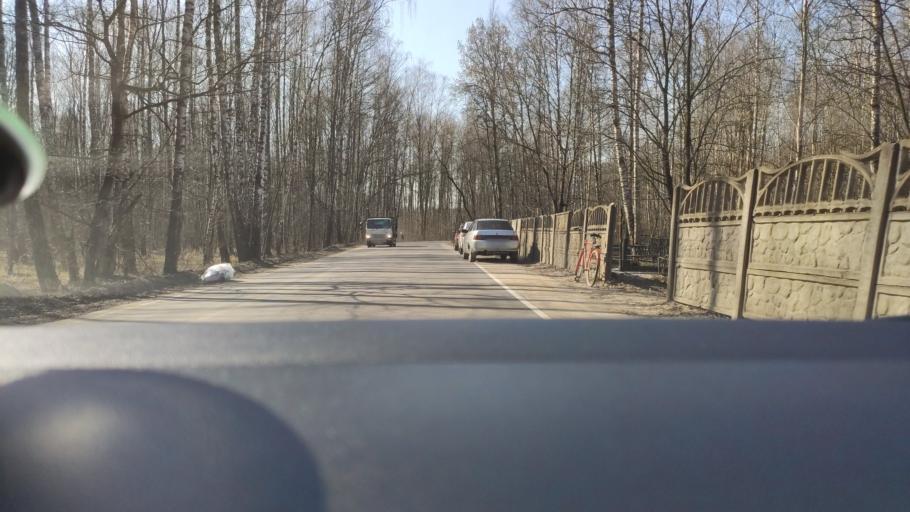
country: RU
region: Moskovskaya
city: Elektrostal'
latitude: 55.7685
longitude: 38.4056
